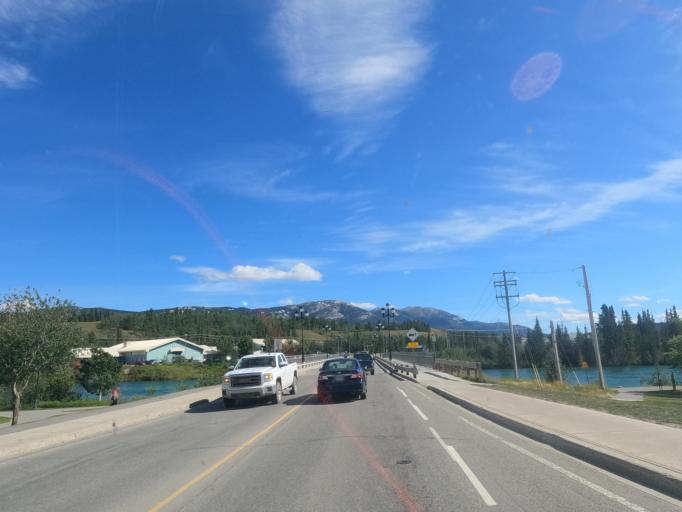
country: CA
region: Yukon
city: Whitehorse
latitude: 60.7142
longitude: -135.0469
